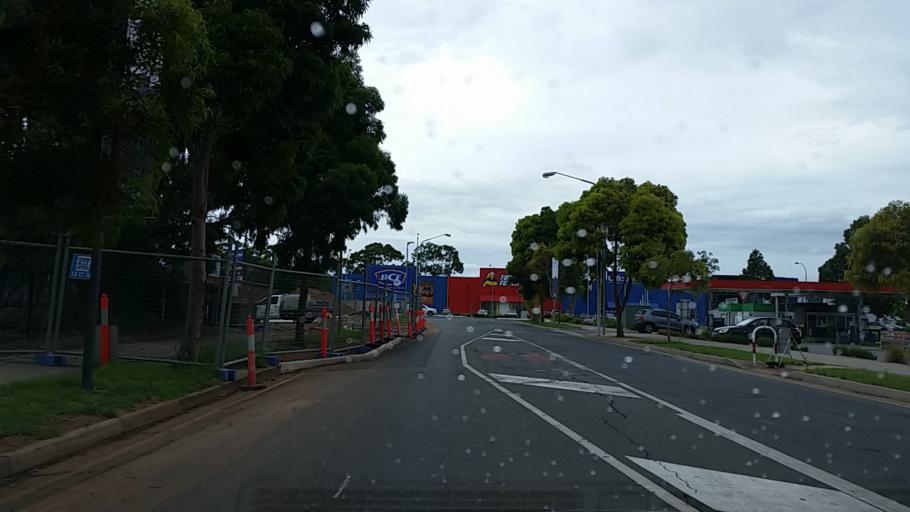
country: AU
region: South Australia
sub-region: Salisbury
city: Elizabeth
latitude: -34.7189
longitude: 138.6712
